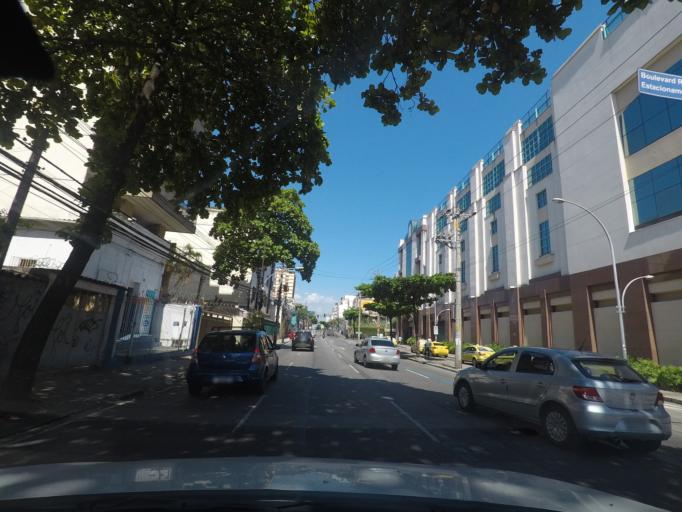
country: BR
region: Rio de Janeiro
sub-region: Rio De Janeiro
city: Rio de Janeiro
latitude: -22.9185
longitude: -43.2507
